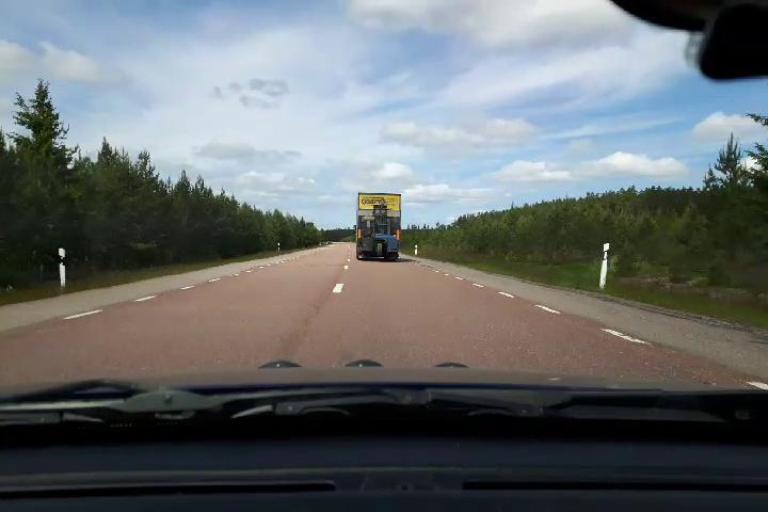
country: SE
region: Uppsala
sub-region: Osthammars Kommun
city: Bjorklinge
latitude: 60.1676
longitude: 17.4907
